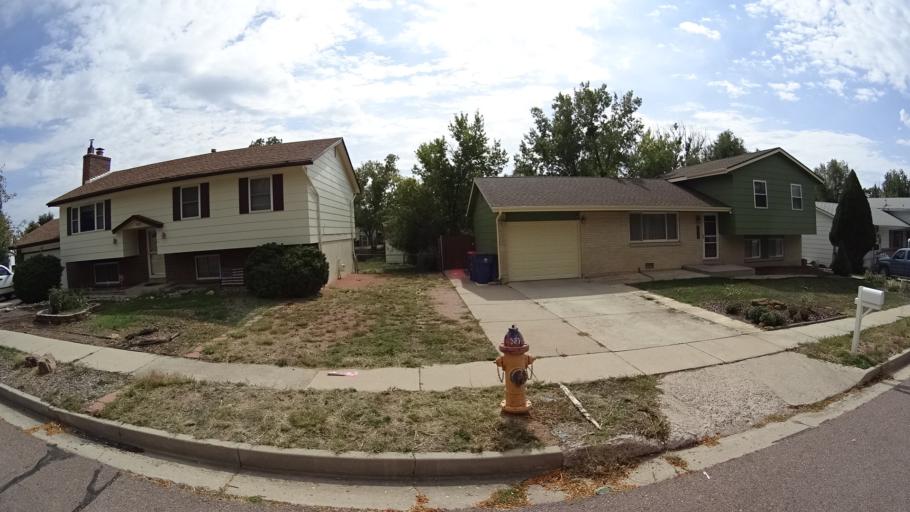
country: US
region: Colorado
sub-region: El Paso County
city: Cimarron Hills
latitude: 38.8607
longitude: -104.7312
